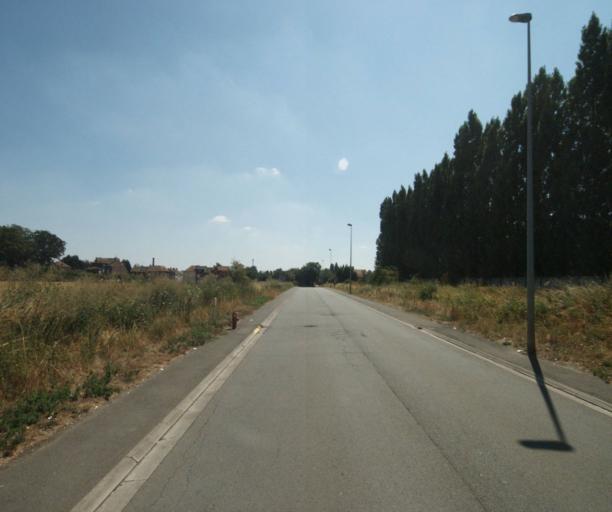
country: FR
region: Nord-Pas-de-Calais
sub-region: Departement du Nord
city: Halluin
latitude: 50.7870
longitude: 3.1163
